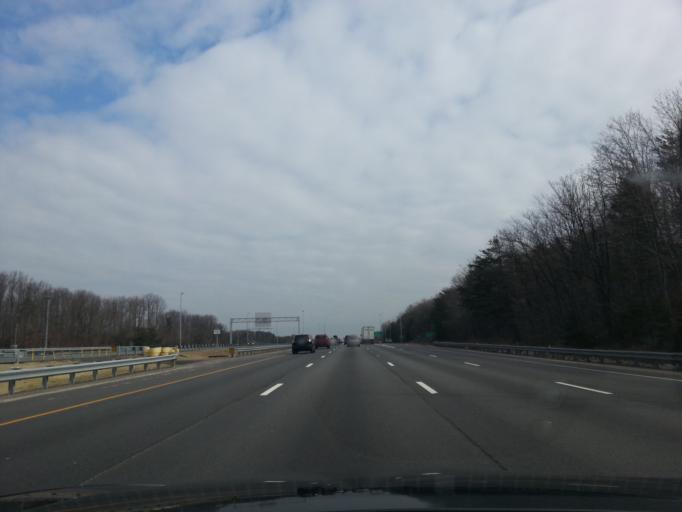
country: US
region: Virginia
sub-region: Prince William County
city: Dale City
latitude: 38.6208
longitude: -77.2963
